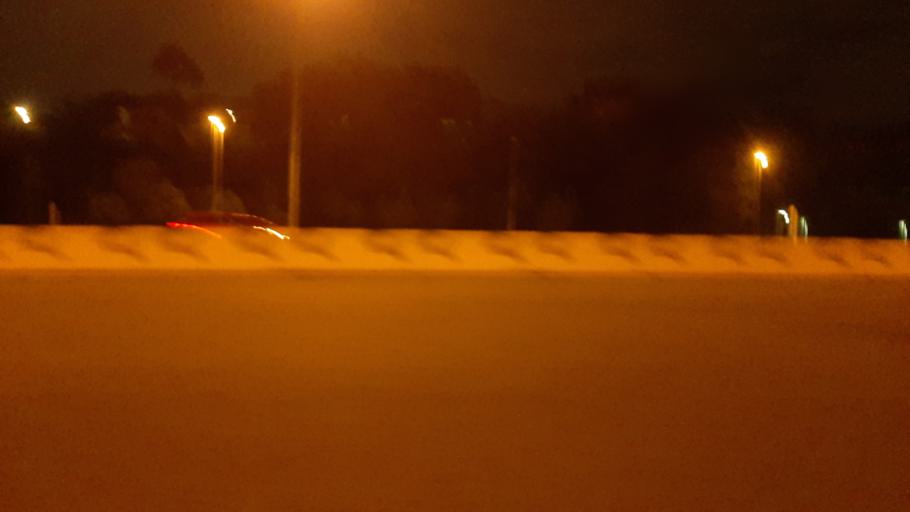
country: MY
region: Kuala Lumpur
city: Kuala Lumpur
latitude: 3.1643
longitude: 101.6423
